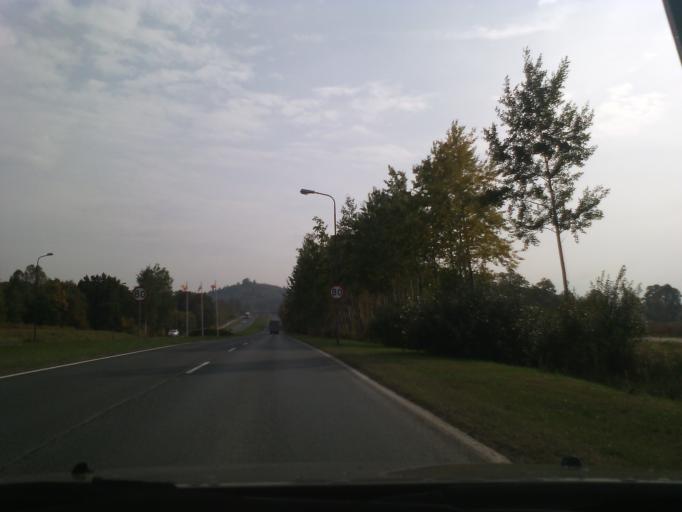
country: PL
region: Lower Silesian Voivodeship
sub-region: Powiat jeleniogorski
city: Jezow Sudecki
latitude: 50.9109
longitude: 15.7851
